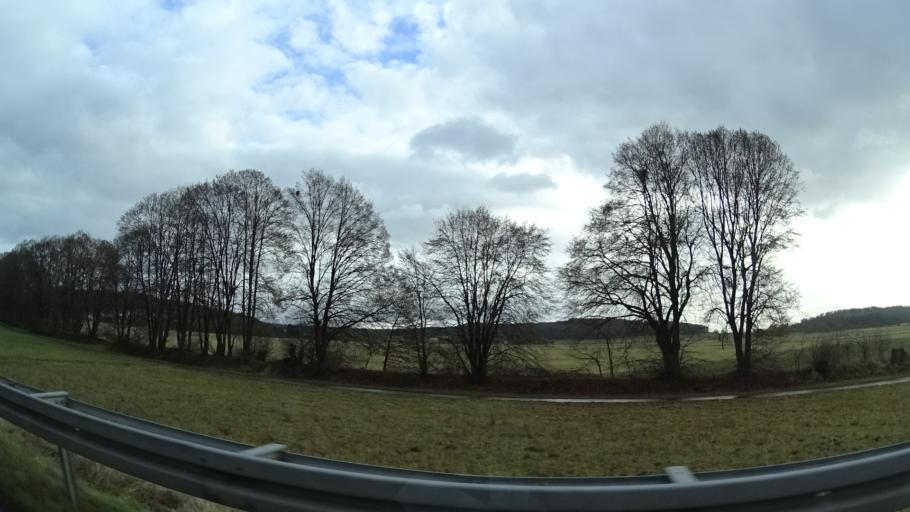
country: DE
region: Hesse
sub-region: Regierungsbezirk Giessen
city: Hungen
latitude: 50.5400
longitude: 8.8922
